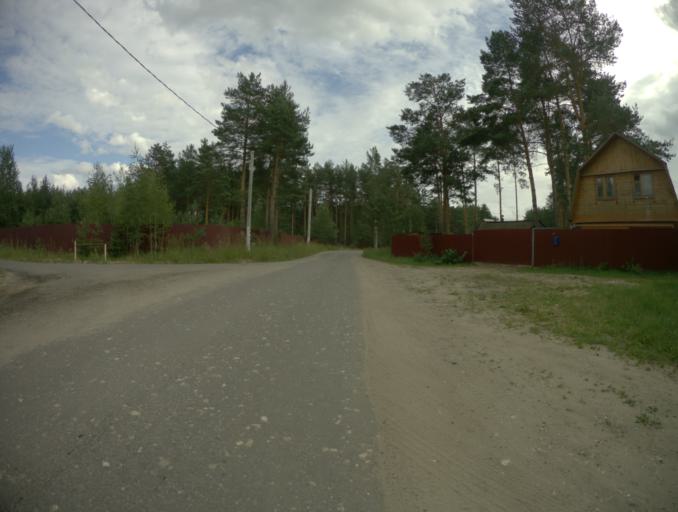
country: RU
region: Vladimir
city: Raduzhnyy
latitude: 56.0293
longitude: 40.3935
